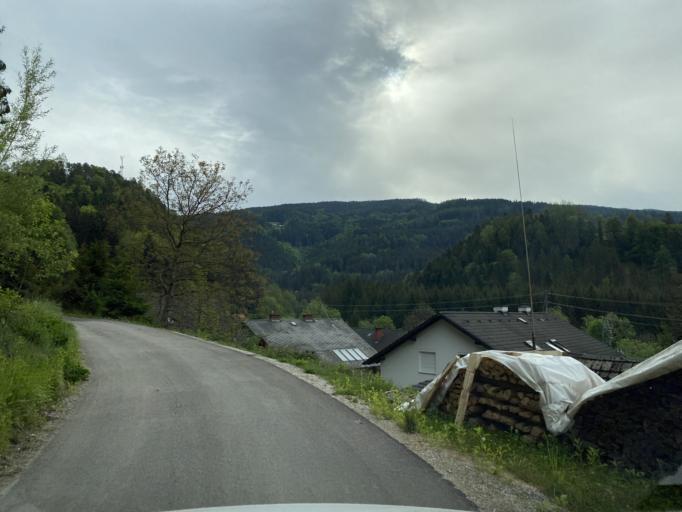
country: AT
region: Styria
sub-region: Politischer Bezirk Weiz
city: Koglhof
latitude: 47.3143
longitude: 15.6844
